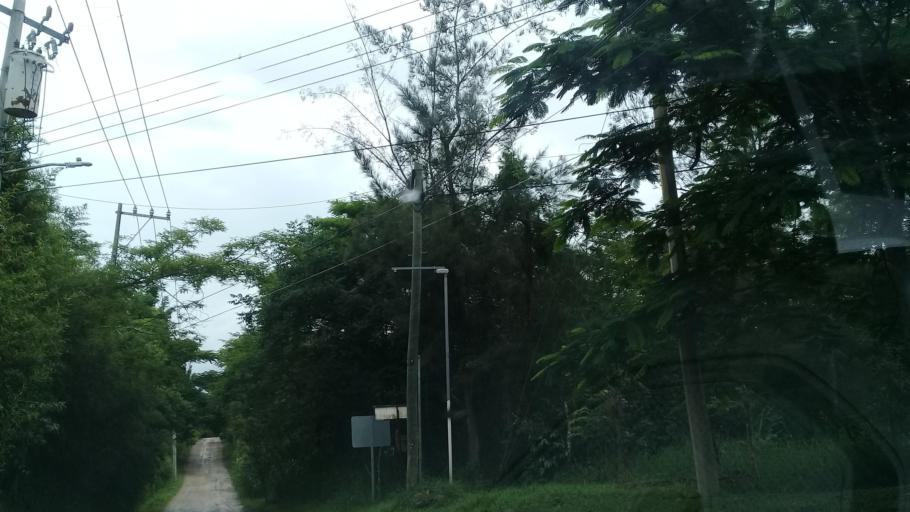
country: MX
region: Veracruz
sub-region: Emiliano Zapata
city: Jacarandas
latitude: 19.5064
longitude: -96.8414
